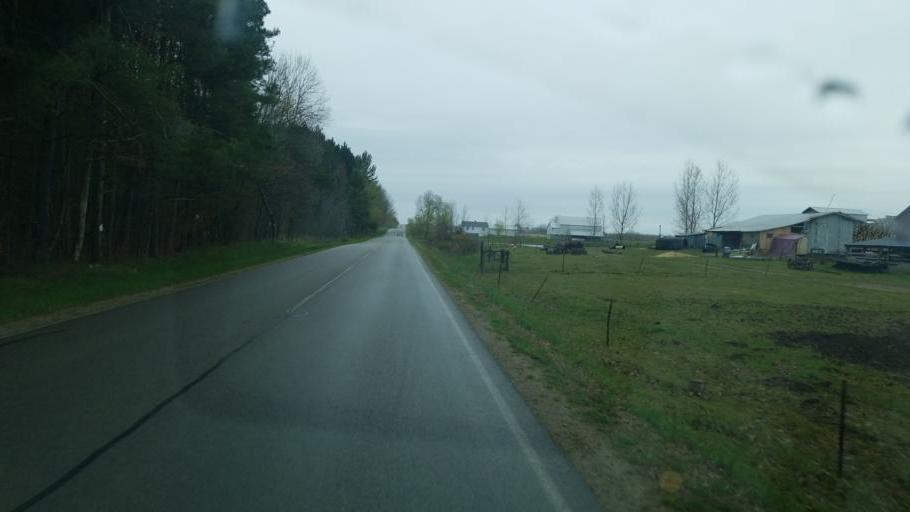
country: US
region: Michigan
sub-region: Montcalm County
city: Lakeview
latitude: 43.4900
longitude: -85.2543
